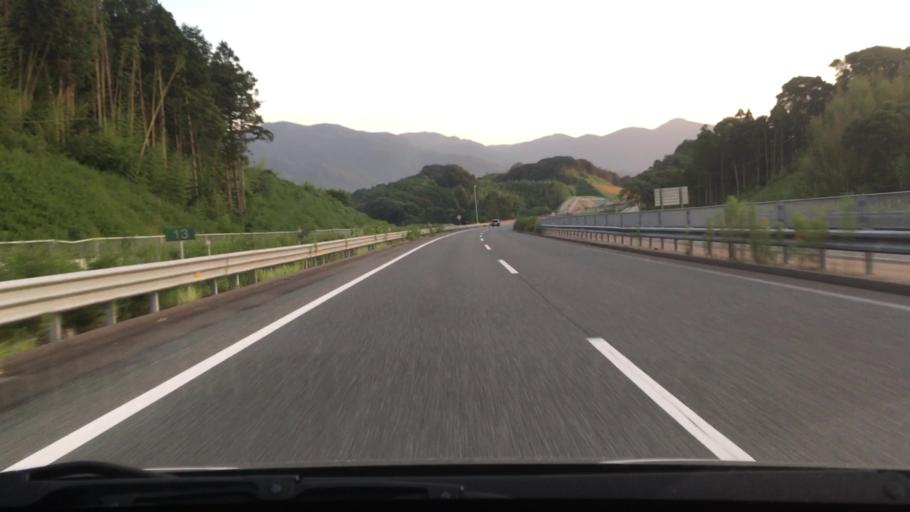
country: JP
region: Fukuoka
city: Maebaru-chuo
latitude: 33.5365
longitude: 130.1953
